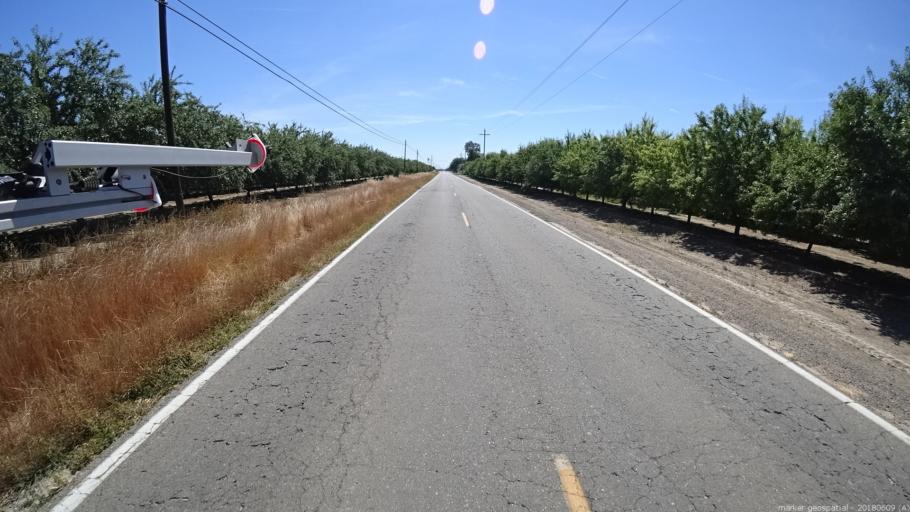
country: US
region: California
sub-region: Madera County
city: Fairmead
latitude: 36.9527
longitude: -120.2060
